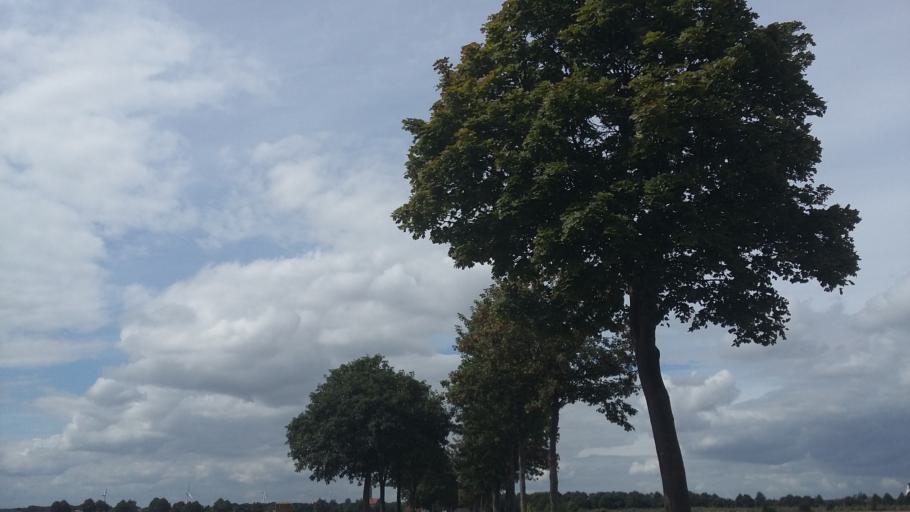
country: DE
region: Lower Saxony
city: Harsum
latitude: 52.2068
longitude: 9.9824
